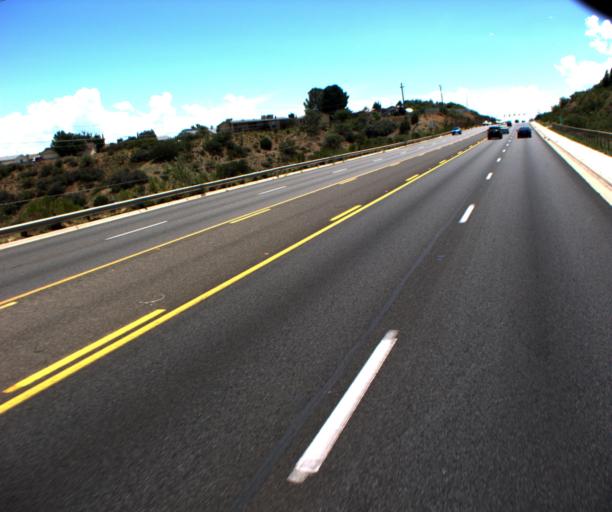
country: US
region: Arizona
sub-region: Yavapai County
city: Verde Village
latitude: 34.7029
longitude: -111.9897
